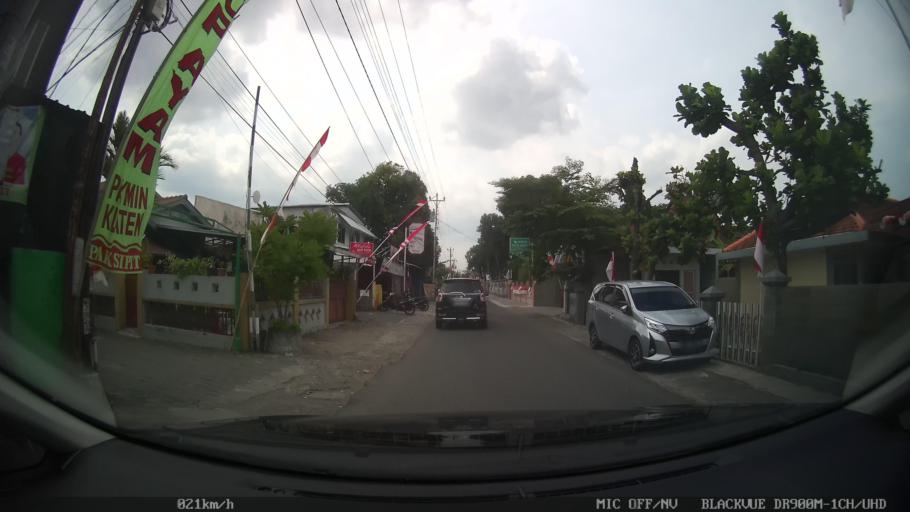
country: ID
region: Daerah Istimewa Yogyakarta
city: Yogyakarta
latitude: -7.7932
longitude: 110.3982
